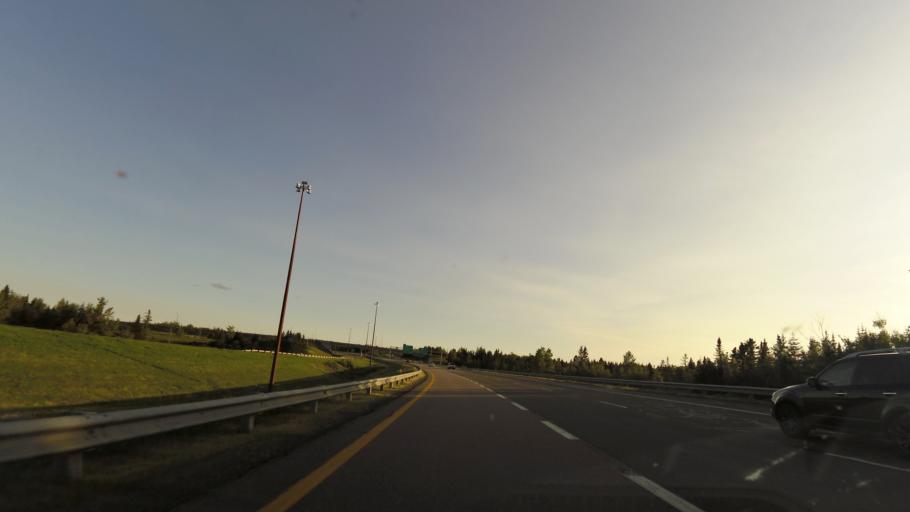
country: CA
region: New Brunswick
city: Salisbury
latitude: 45.9963
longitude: -65.1382
